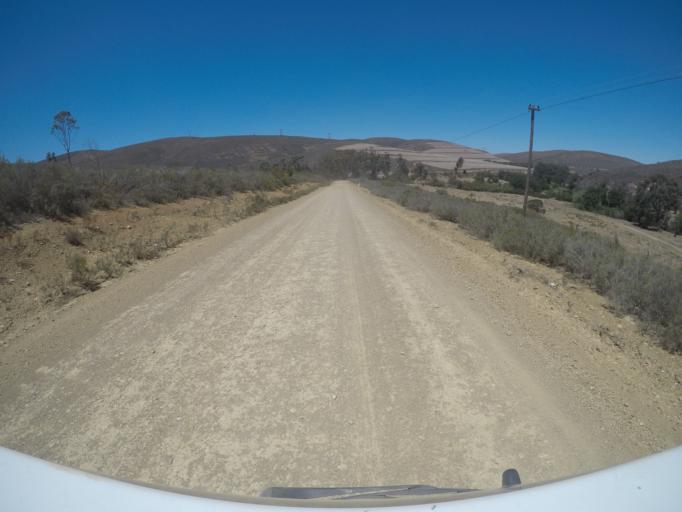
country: ZA
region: Western Cape
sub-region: Overberg District Municipality
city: Caledon
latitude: -34.1361
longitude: 19.2454
